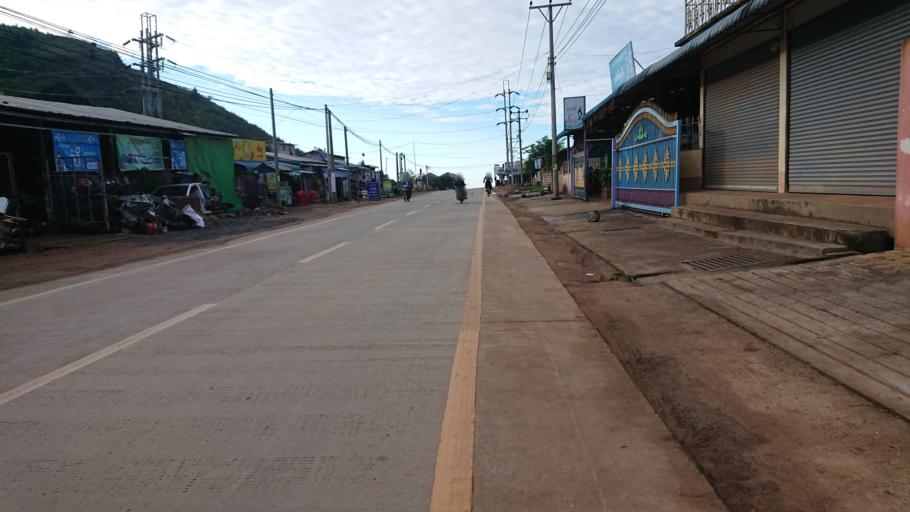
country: MM
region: Shan
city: Taunggyi
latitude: 20.7453
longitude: 97.0506
